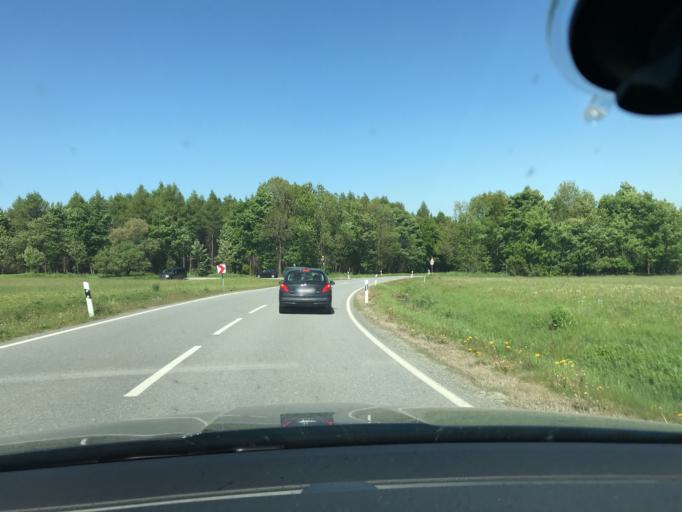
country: CZ
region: Ustecky
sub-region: Okres Chomutov
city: Vejprty
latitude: 50.4526
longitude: 13.0045
